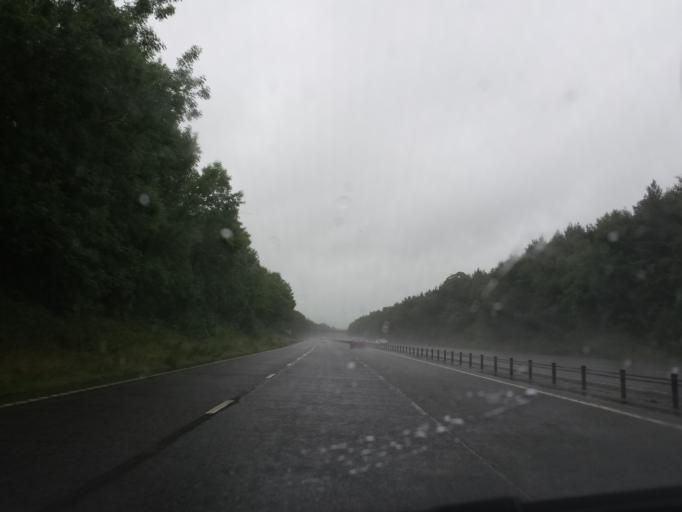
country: GB
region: England
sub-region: Warwickshire
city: Kenilworth
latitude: 52.3412
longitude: -1.5498
